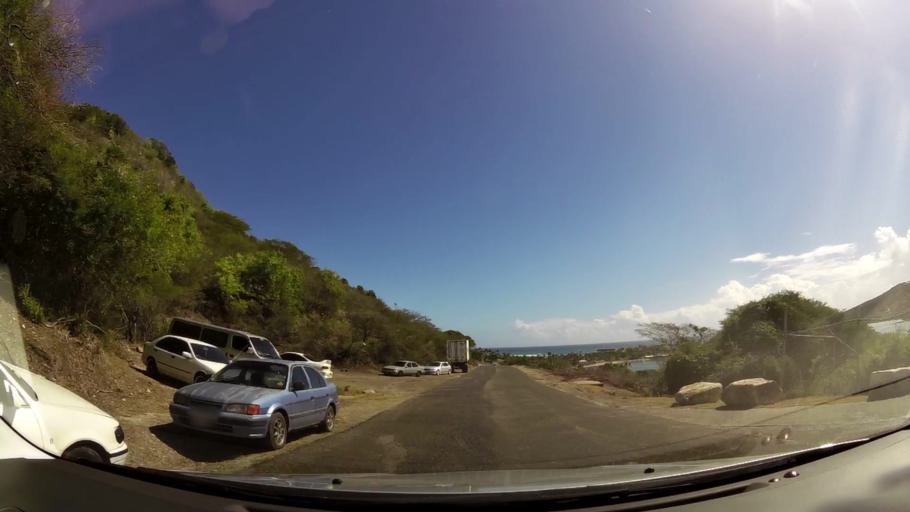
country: AG
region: Saint Paul
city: Falmouth
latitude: 17.0190
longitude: -61.7387
